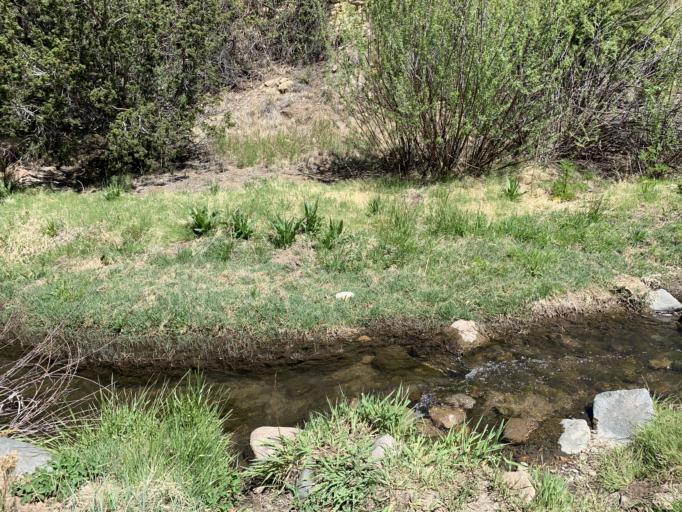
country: US
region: New Mexico
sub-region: Lincoln County
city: Capitan
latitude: 33.4675
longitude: -105.5804
